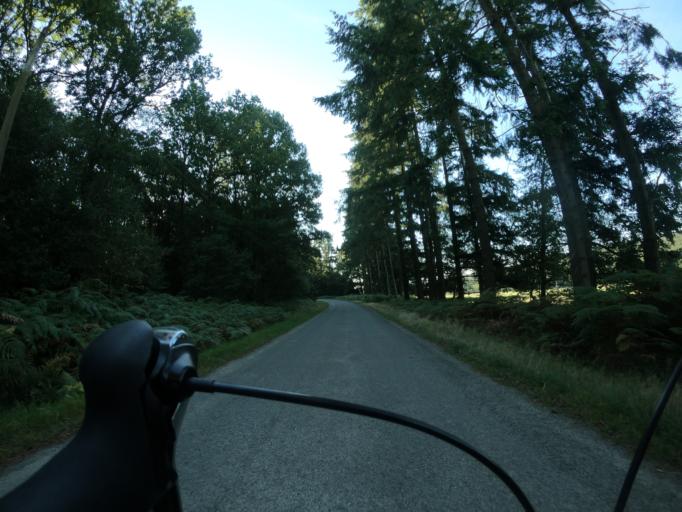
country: FR
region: Lower Normandy
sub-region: Departement de l'Orne
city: Magny-le-Desert
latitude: 48.5334
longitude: -0.2745
